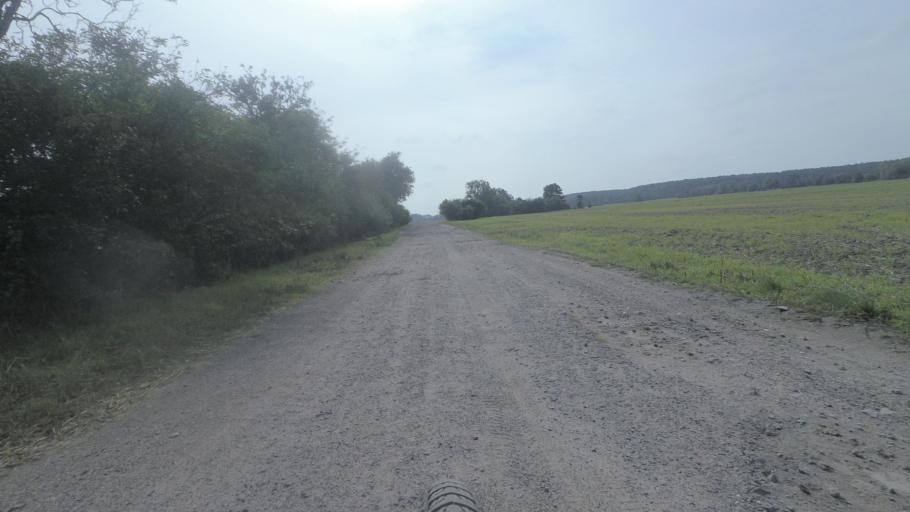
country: DE
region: Brandenburg
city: Rangsdorf
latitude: 52.2783
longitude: 13.3865
